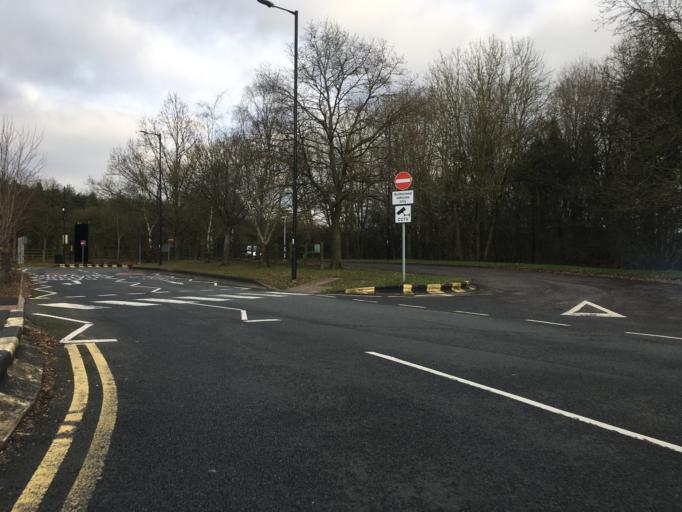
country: GB
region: England
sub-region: South Gloucestershire
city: Charfield
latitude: 51.6577
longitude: -2.4248
